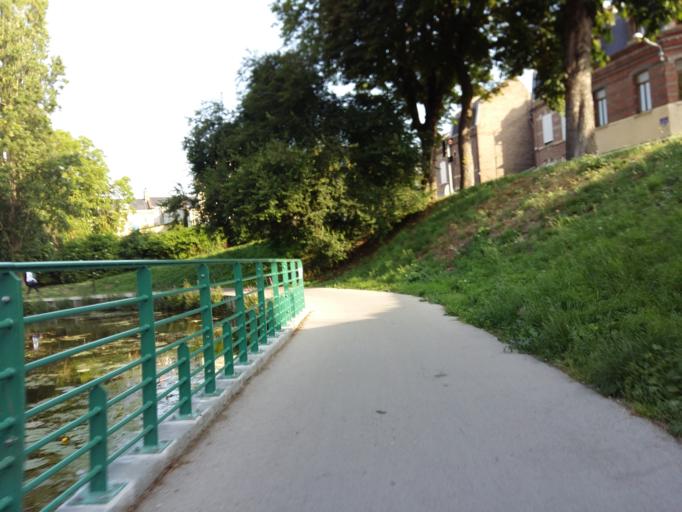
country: FR
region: Picardie
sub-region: Departement de la Somme
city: Amiens
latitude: 49.9020
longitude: 2.2963
